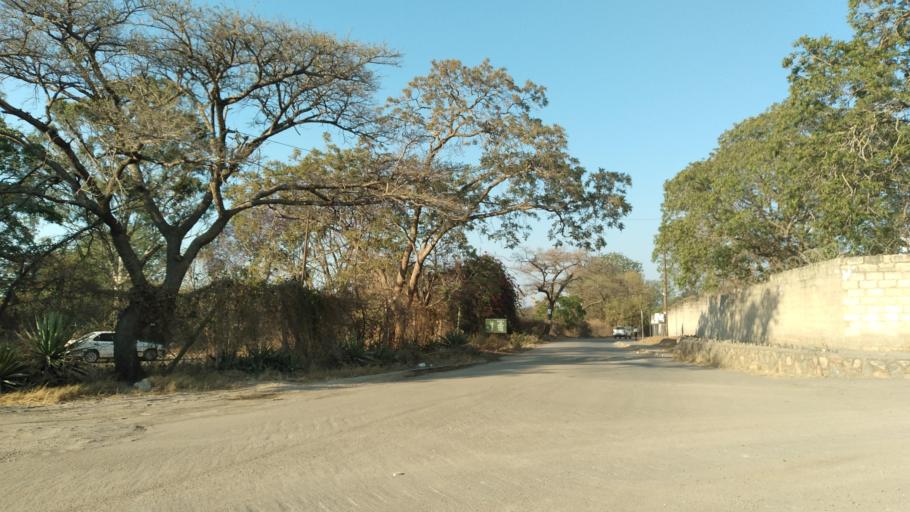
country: ZM
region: Lusaka
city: Lusaka
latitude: -15.5475
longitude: 28.2731
